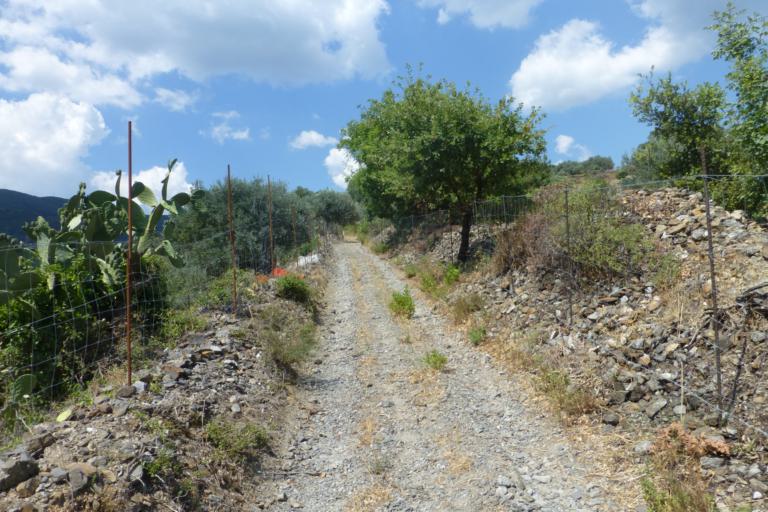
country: IT
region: Calabria
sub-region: Provincia di Reggio Calabria
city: Pazzano
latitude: 38.4799
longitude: 16.4418
